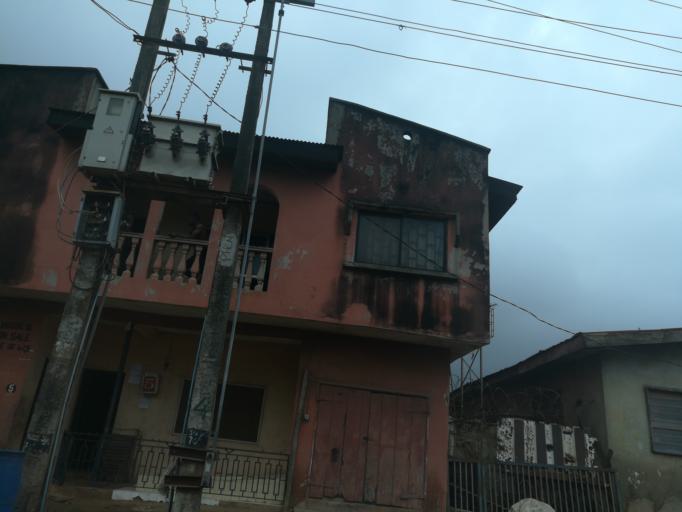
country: NG
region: Lagos
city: Agege
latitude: 6.6086
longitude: 3.3287
